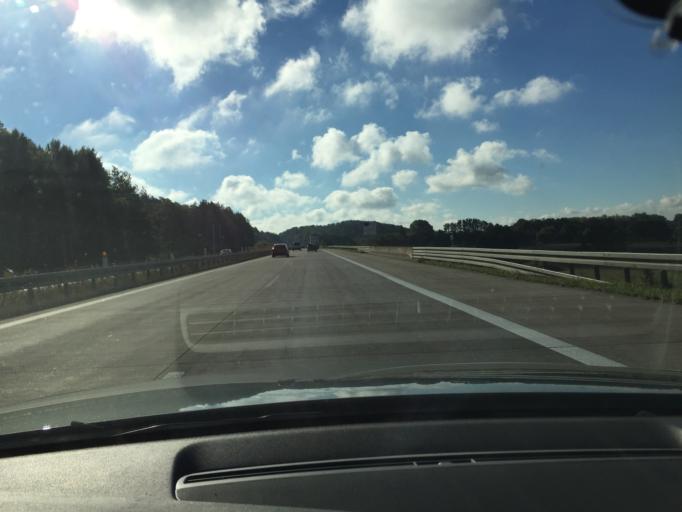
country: DE
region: Mecklenburg-Vorpommern
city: Lalendorf
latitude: 53.7610
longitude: 12.3258
